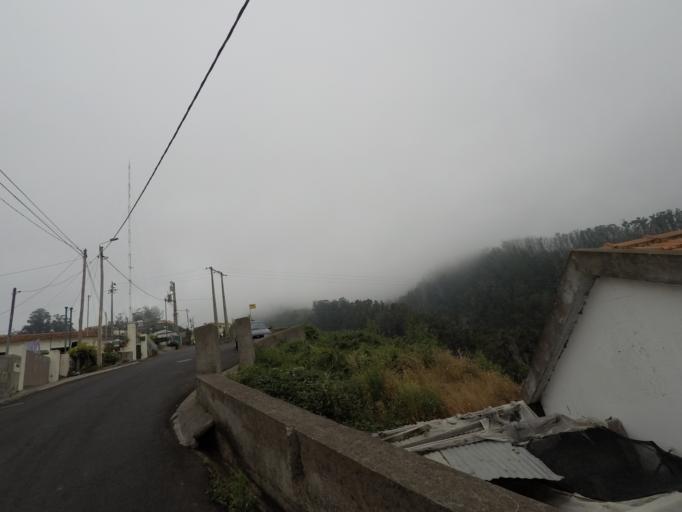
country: PT
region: Madeira
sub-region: Camara de Lobos
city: Curral das Freiras
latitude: 32.6825
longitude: -16.9470
